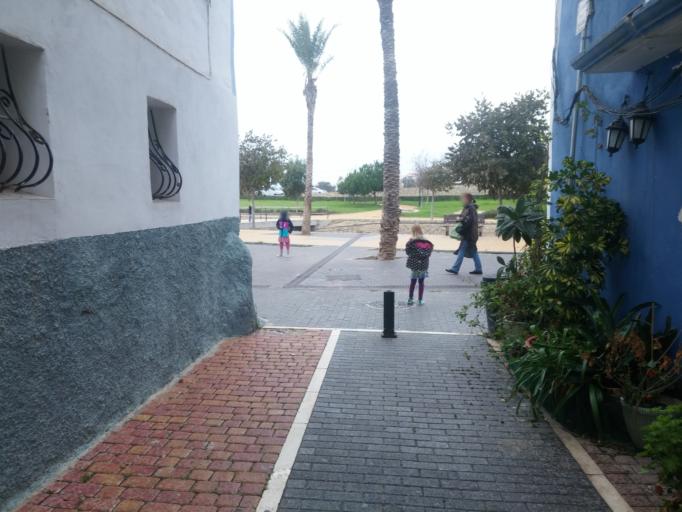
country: ES
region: Valencia
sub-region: Provincia de Alicante
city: Villajoyosa
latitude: 38.5033
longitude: -0.2332
